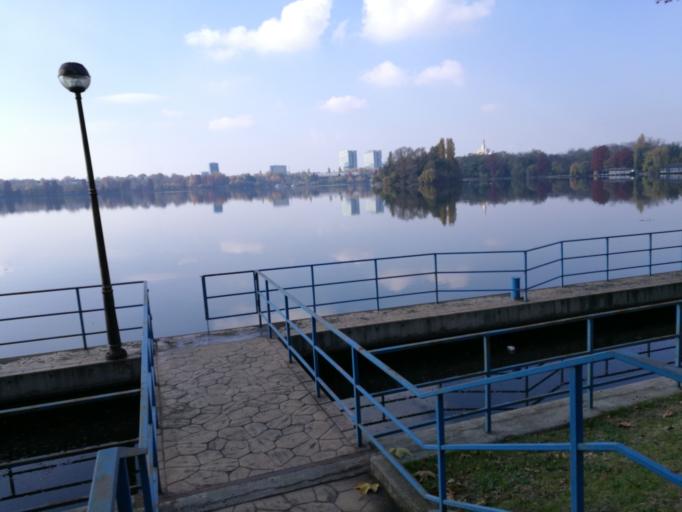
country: RO
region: Bucuresti
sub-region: Municipiul Bucuresti
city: Bucharest
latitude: 44.4755
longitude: 26.0889
